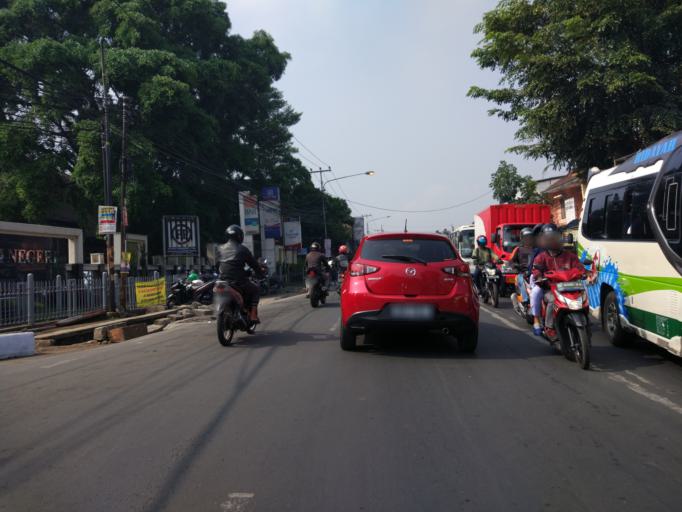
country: ID
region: West Java
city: Cileunyi
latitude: -6.9325
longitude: 107.7158
